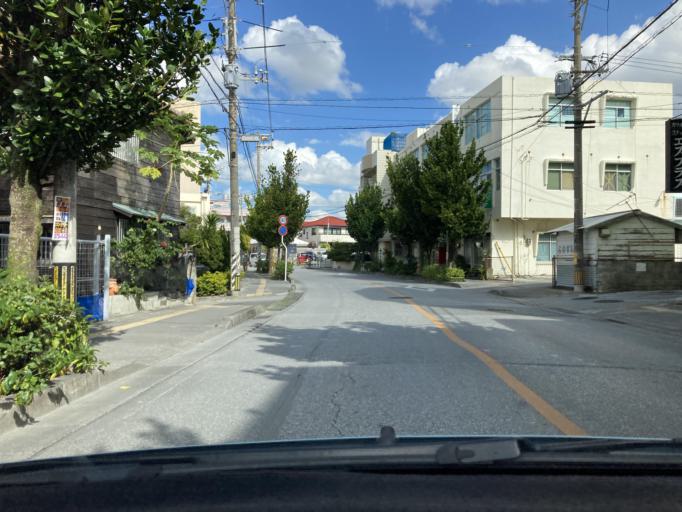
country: JP
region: Okinawa
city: Naha-shi
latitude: 26.2109
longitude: 127.6991
